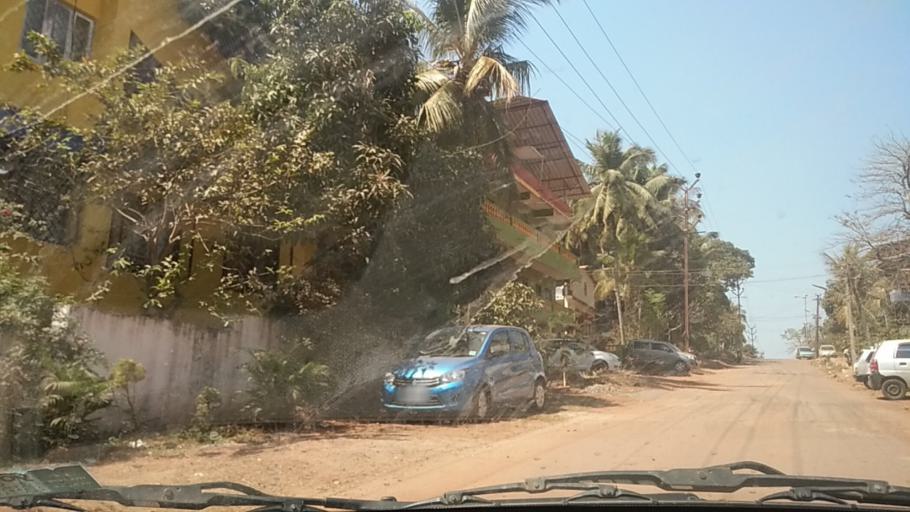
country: IN
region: Goa
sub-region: North Goa
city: Panaji
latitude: 15.5137
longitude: 73.8385
